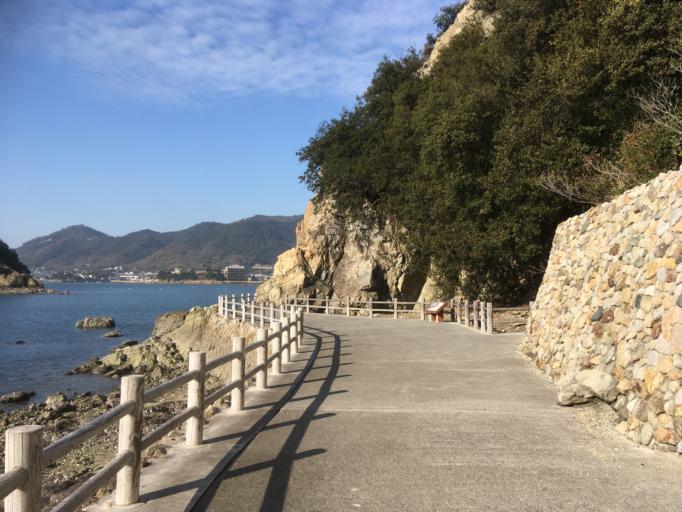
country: JP
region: Hiroshima
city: Fukuyama
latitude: 34.3823
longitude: 133.3930
